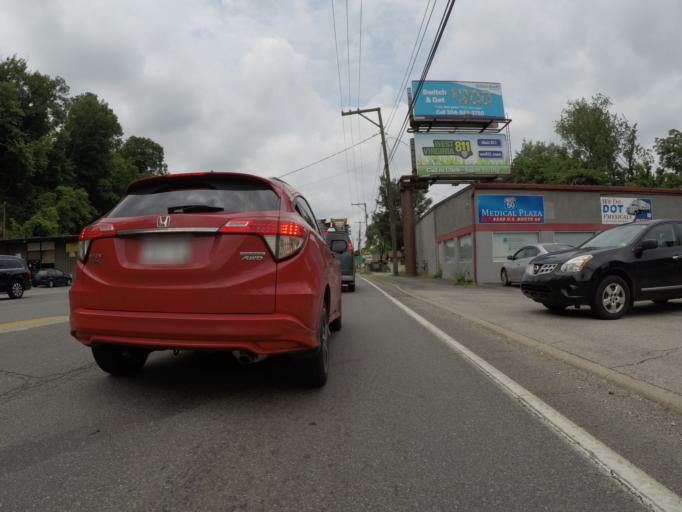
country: US
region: West Virginia
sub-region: Cabell County
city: Pea Ridge
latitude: 38.4129
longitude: -82.3589
